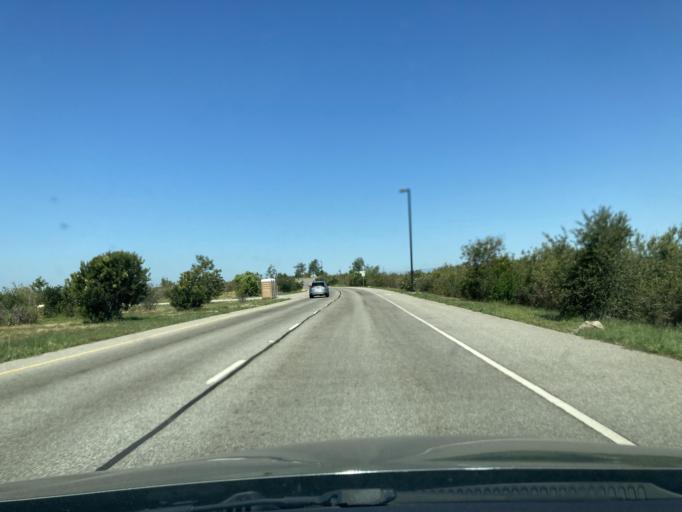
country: US
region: California
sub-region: Ventura County
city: Camarillo
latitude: 34.1690
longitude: -119.0504
